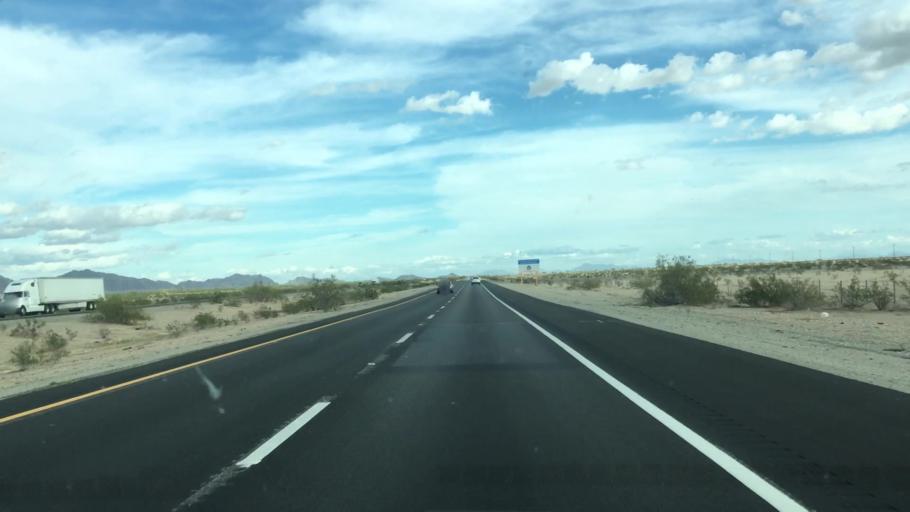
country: US
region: California
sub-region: Riverside County
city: Mesa Verde
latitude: 33.6090
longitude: -114.8793
